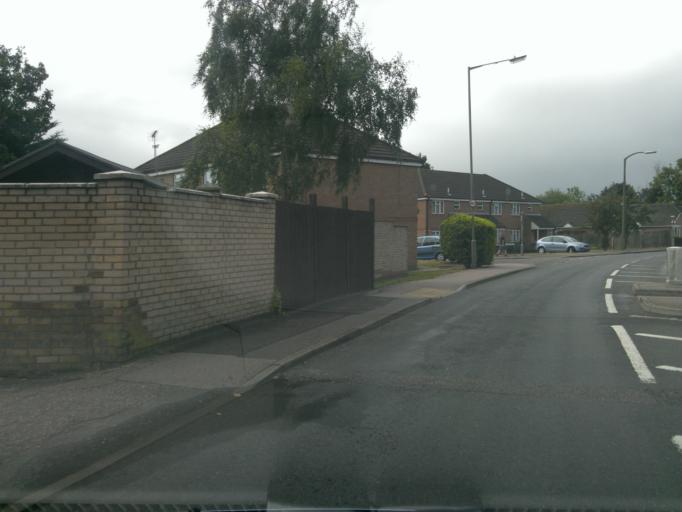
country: GB
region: England
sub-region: Essex
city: Little Clacton
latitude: 51.8124
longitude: 1.1522
